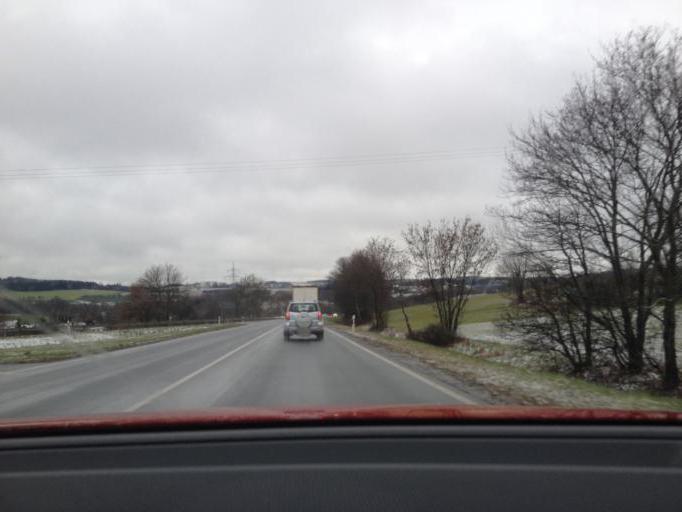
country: DE
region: Bavaria
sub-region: Upper Franconia
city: Dohlau
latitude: 50.2852
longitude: 11.9437
